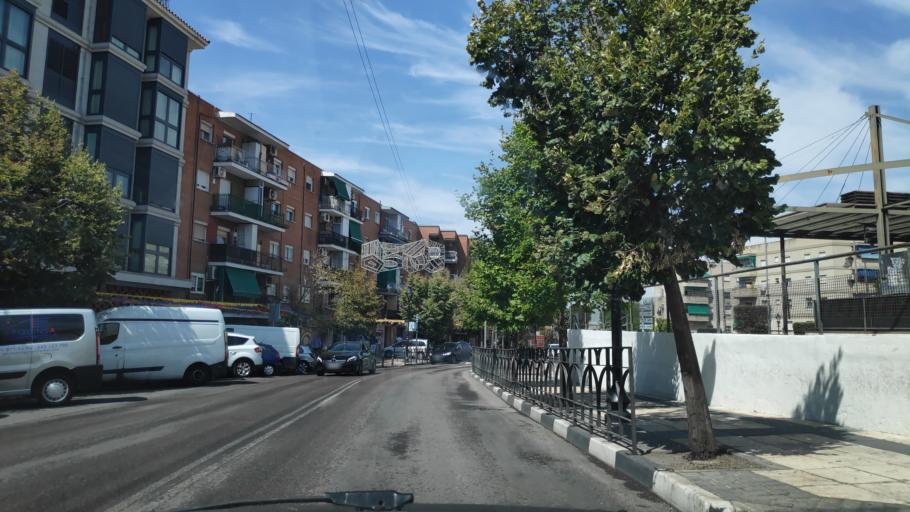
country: ES
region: Madrid
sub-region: Provincia de Madrid
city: Arganda
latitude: 40.3024
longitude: -3.4420
